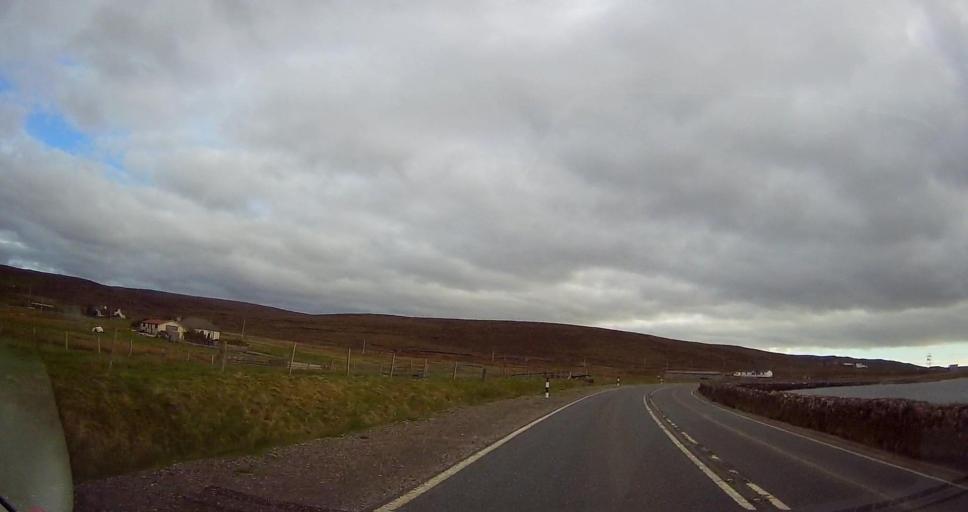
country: GB
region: Scotland
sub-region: Shetland Islands
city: Lerwick
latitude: 60.4446
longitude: -1.2590
